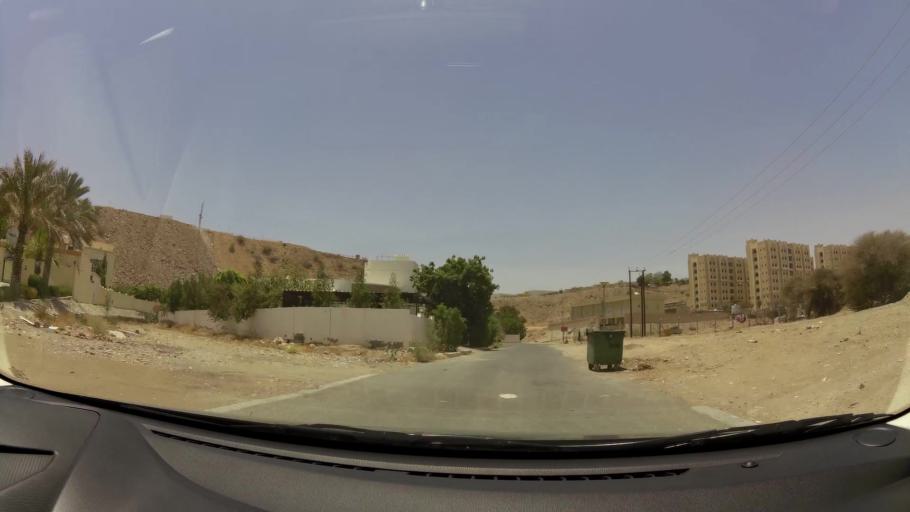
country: OM
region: Muhafazat Masqat
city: Bawshar
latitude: 23.6038
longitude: 58.4640
